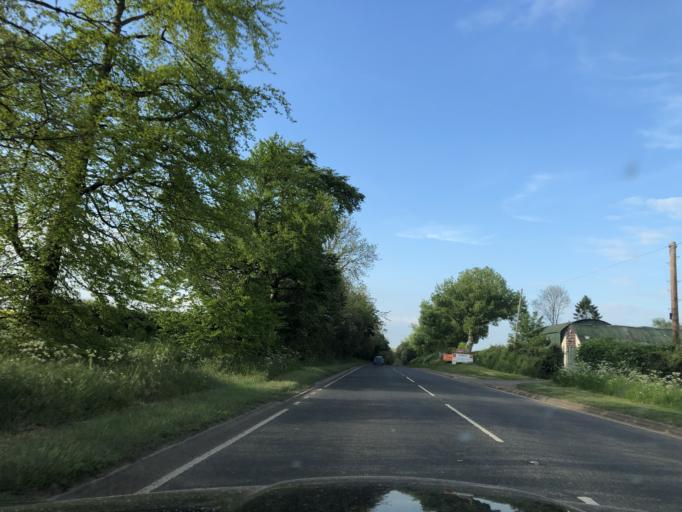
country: GB
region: England
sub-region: Warwickshire
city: Shipston on Stour
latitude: 52.1002
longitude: -1.6268
